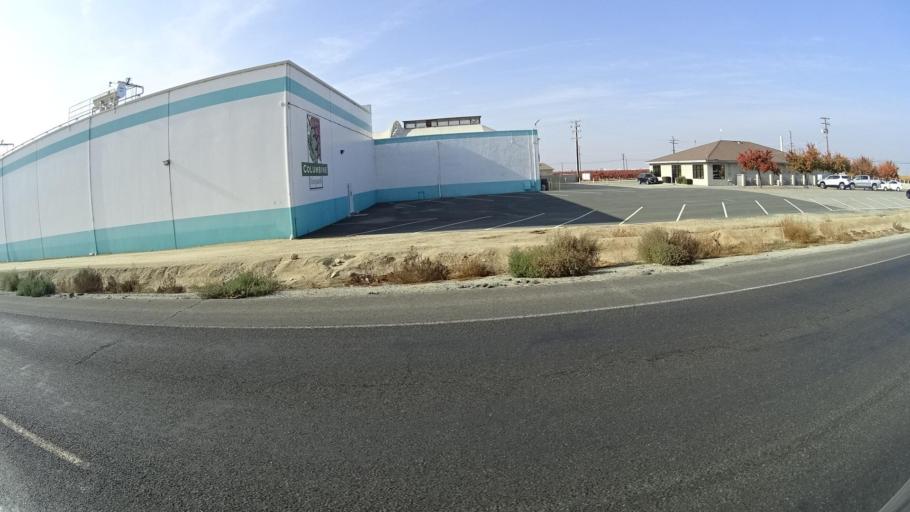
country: US
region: California
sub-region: Tulare County
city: Richgrove
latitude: 35.7746
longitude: -119.1247
